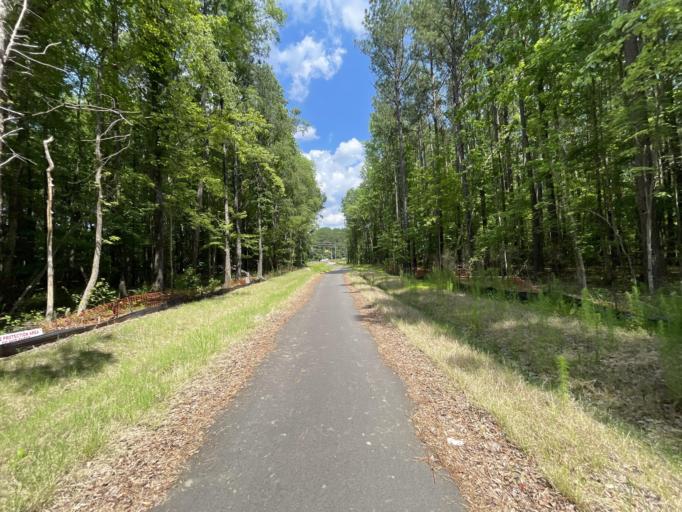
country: US
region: North Carolina
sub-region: Wake County
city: Morrisville
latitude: 35.8170
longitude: -78.8494
